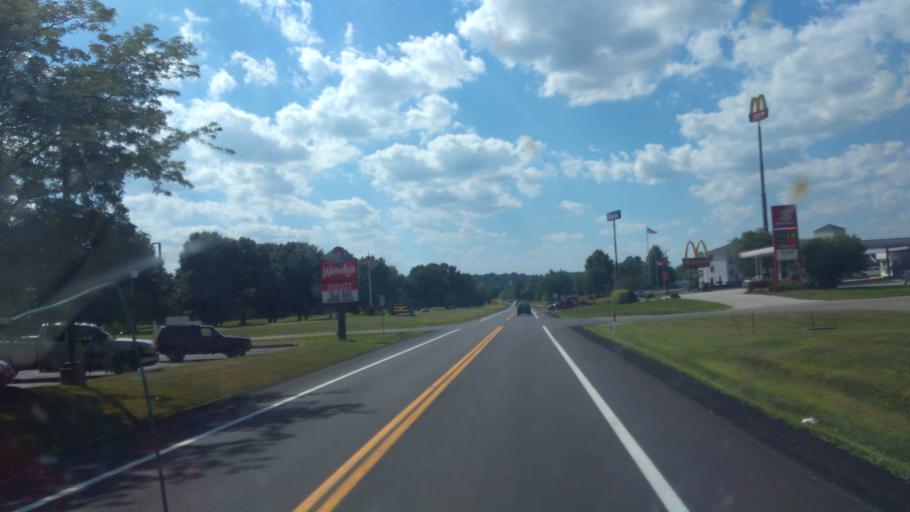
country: US
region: Ohio
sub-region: Tuscarawas County
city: Strasburg
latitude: 40.6400
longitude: -81.4430
